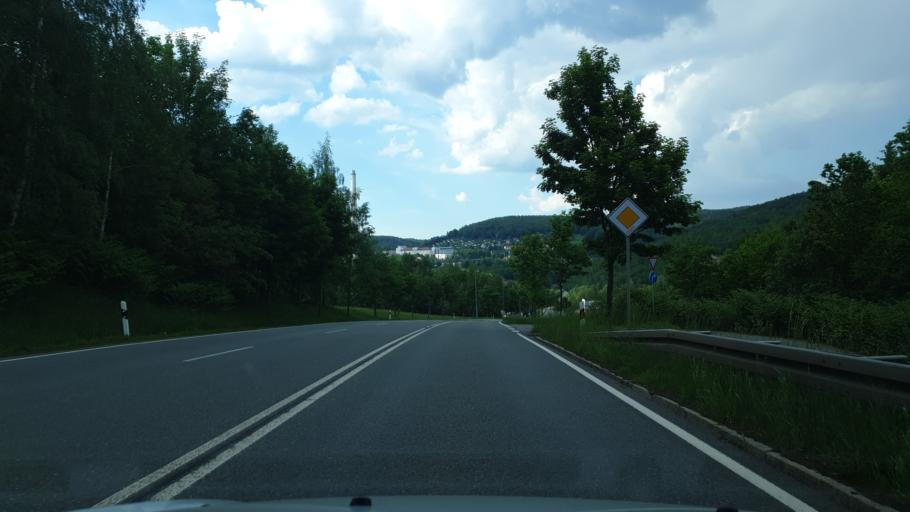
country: DE
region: Saxony
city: Aue
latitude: 50.5774
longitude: 12.7183
